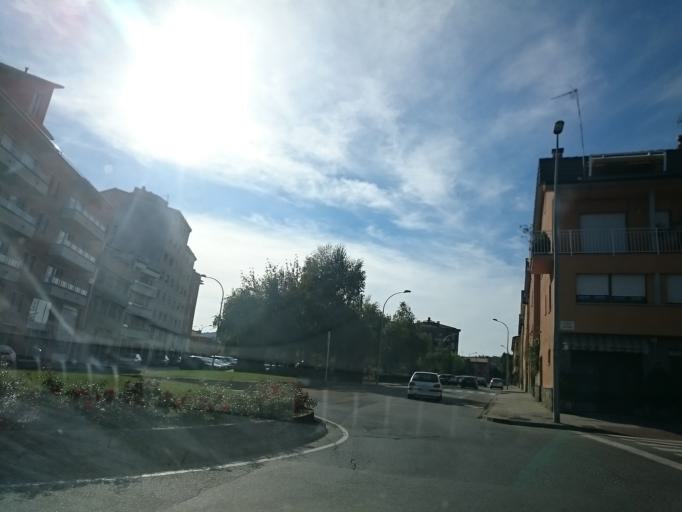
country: ES
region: Catalonia
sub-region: Provincia de Barcelona
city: Vic
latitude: 41.9204
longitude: 2.2590
